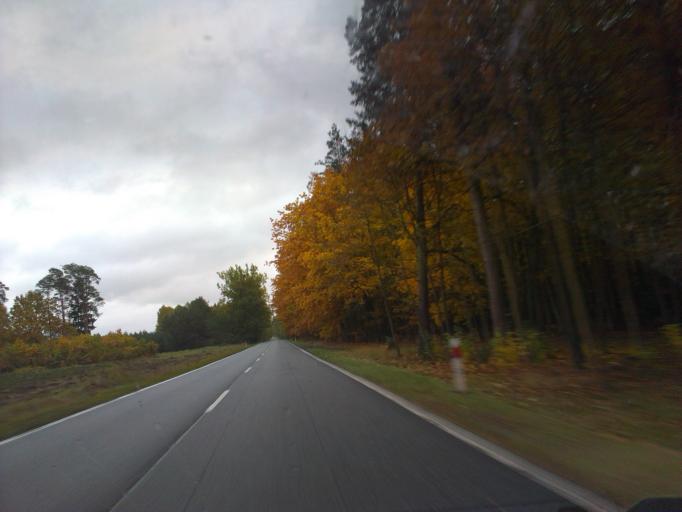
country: PL
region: Kujawsko-Pomorskie
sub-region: Powiat swiecki
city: Lniano
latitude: 53.4676
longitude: 18.1705
